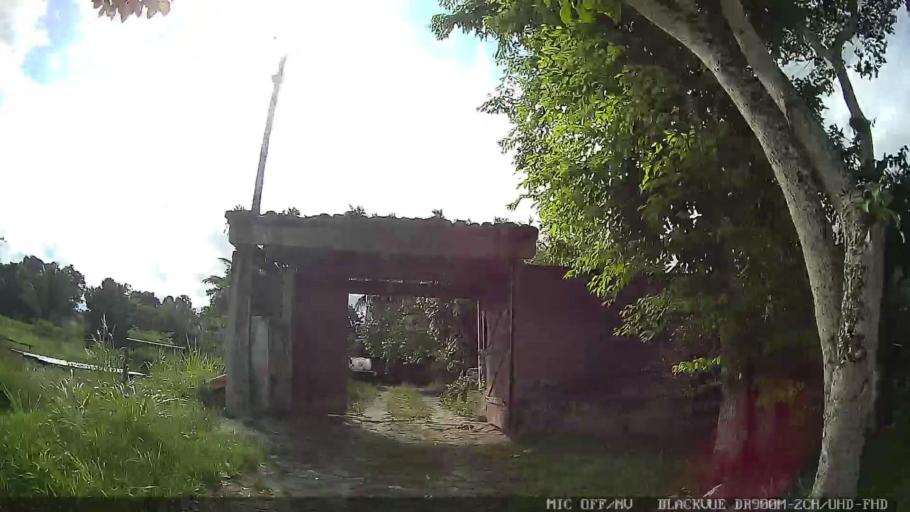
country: BR
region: Sao Paulo
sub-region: Caraguatatuba
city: Caraguatatuba
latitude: -23.6444
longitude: -45.4452
